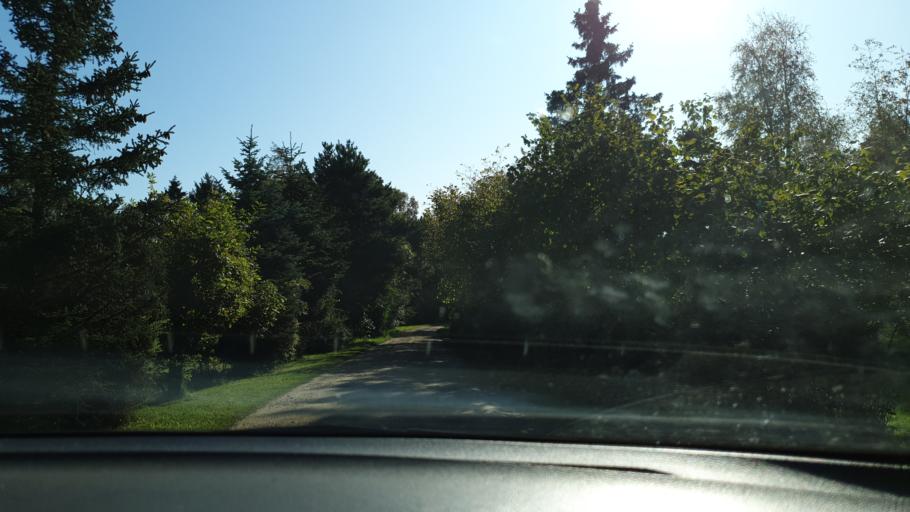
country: DK
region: Zealand
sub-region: Odsherred Kommune
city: Hojby
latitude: 55.9356
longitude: 11.6257
